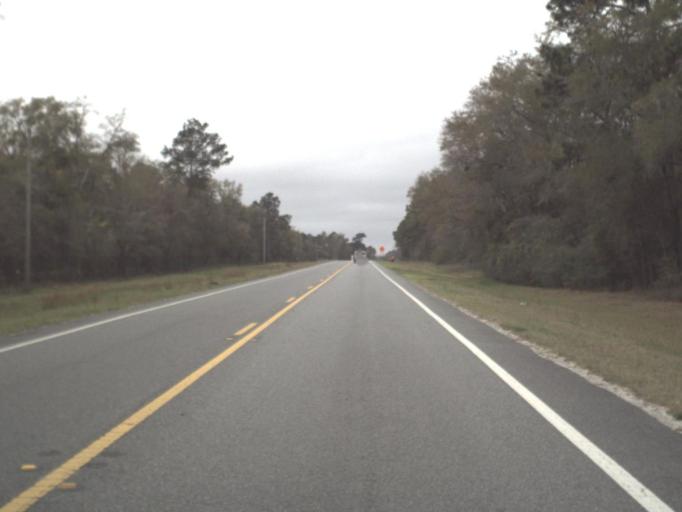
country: US
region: Florida
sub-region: Wakulla County
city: Crawfordville
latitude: 30.1428
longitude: -84.3060
